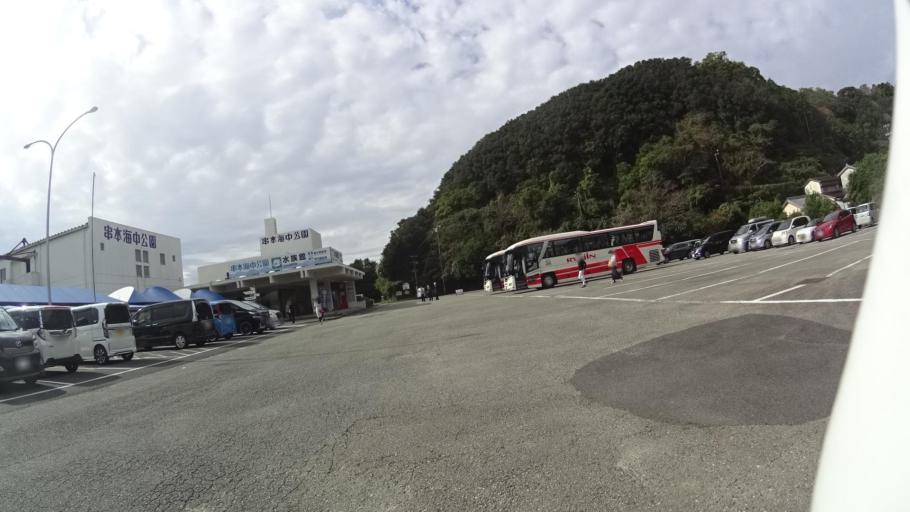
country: JP
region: Wakayama
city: Shingu
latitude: 33.4814
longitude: 135.7450
